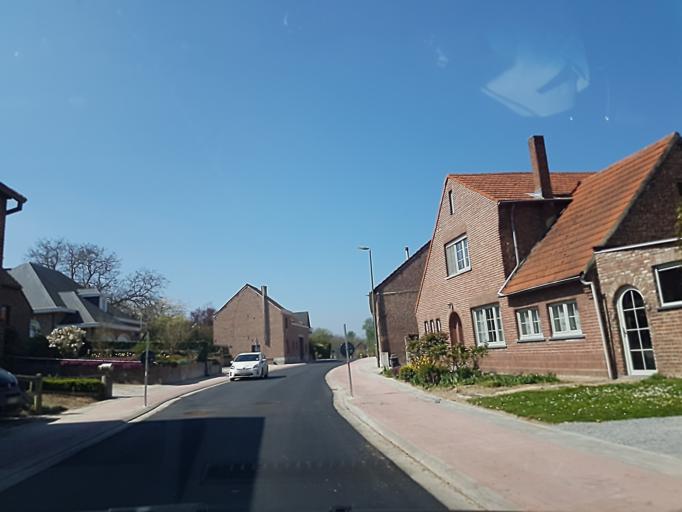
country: BE
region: Flanders
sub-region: Provincie Vlaams-Brabant
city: Oud-Heverlee
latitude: 50.8235
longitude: 4.6727
